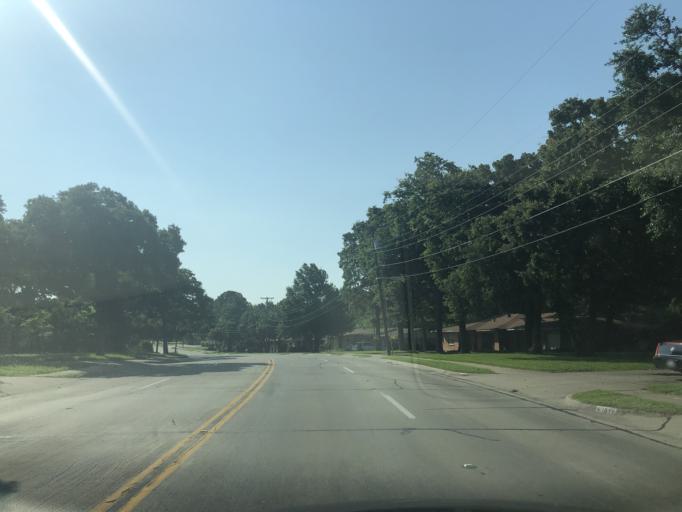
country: US
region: Texas
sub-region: Dallas County
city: Irving
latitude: 32.8093
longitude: -96.9660
